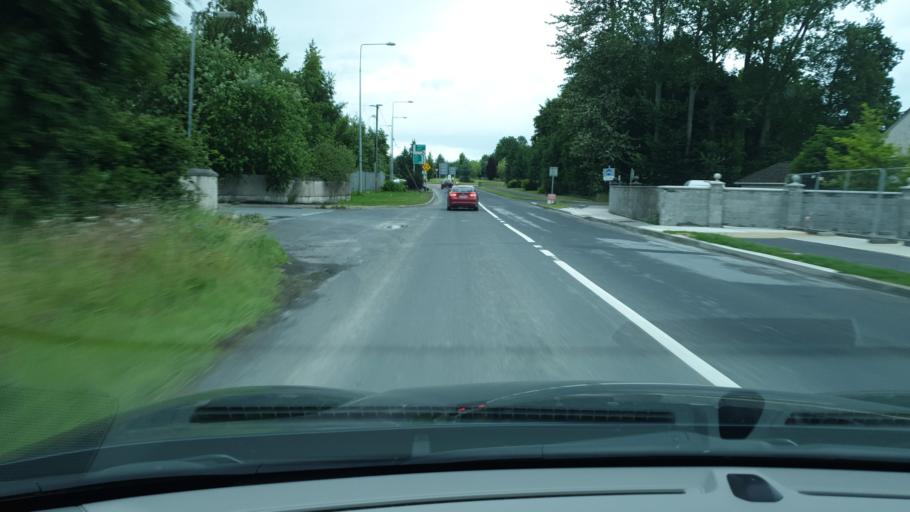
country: IE
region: Leinster
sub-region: An Mhi
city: Navan
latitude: 53.6487
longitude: -6.7062
